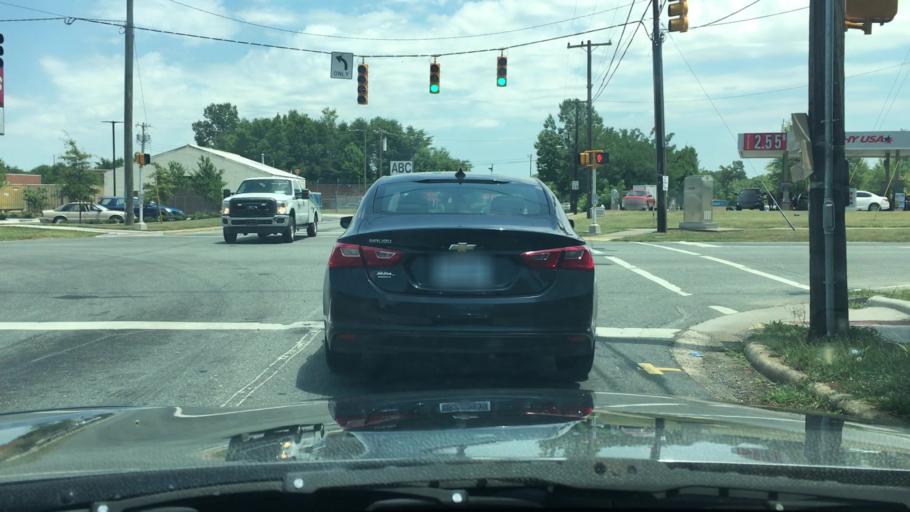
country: US
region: North Carolina
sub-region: Alamance County
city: Graham
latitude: 36.0933
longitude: -79.4062
